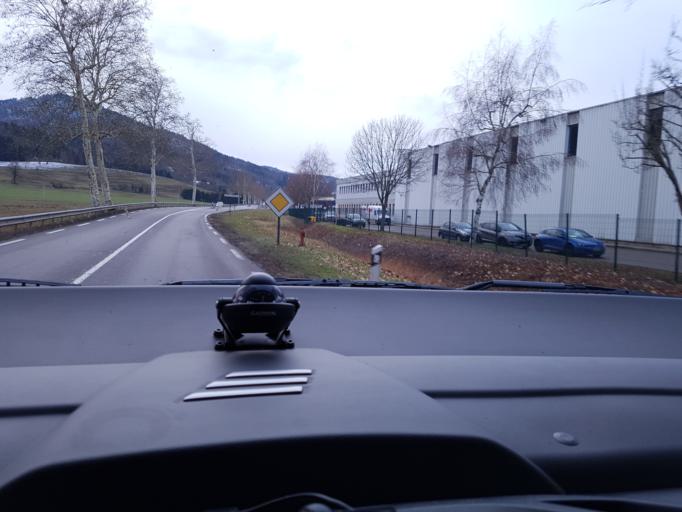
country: FR
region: Alsace
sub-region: Departement du Haut-Rhin
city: Liepvre
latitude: 48.2707
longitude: 7.3279
